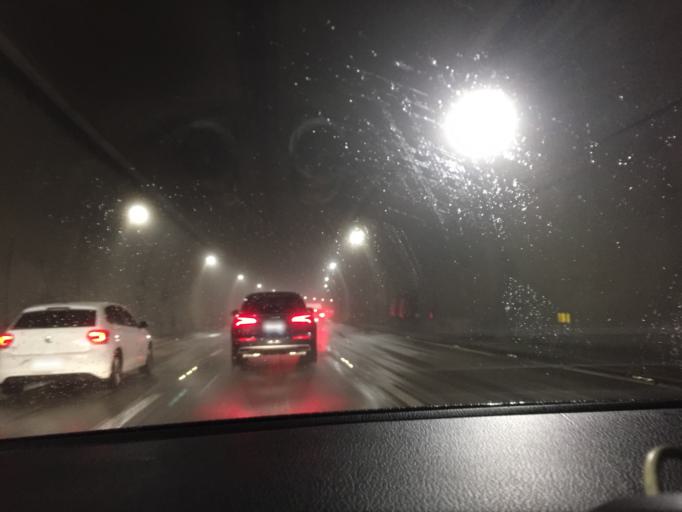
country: BR
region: Sao Paulo
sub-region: Cubatao
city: Cubatao
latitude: -23.9171
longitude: -46.5297
